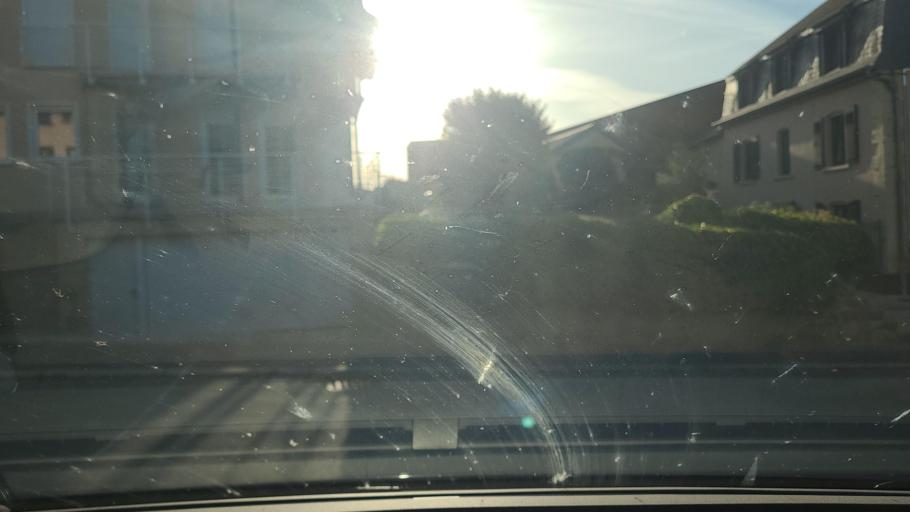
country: LU
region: Luxembourg
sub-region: Canton de Capellen
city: Garnich
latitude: 49.6152
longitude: 5.9544
